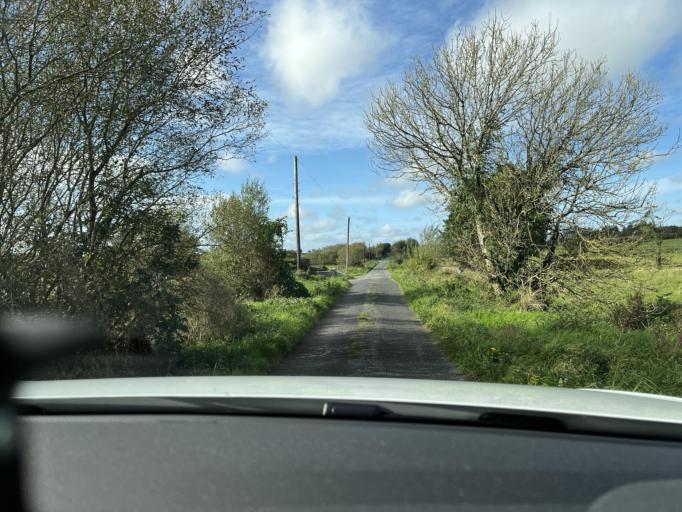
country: IE
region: Connaught
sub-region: Sligo
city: Ballymote
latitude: 54.0728
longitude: -8.4318
